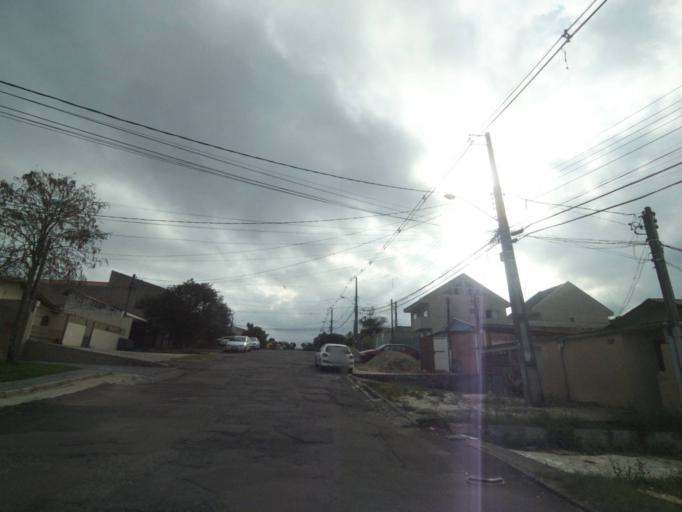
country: BR
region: Parana
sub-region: Pinhais
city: Pinhais
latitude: -25.4074
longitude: -49.2051
